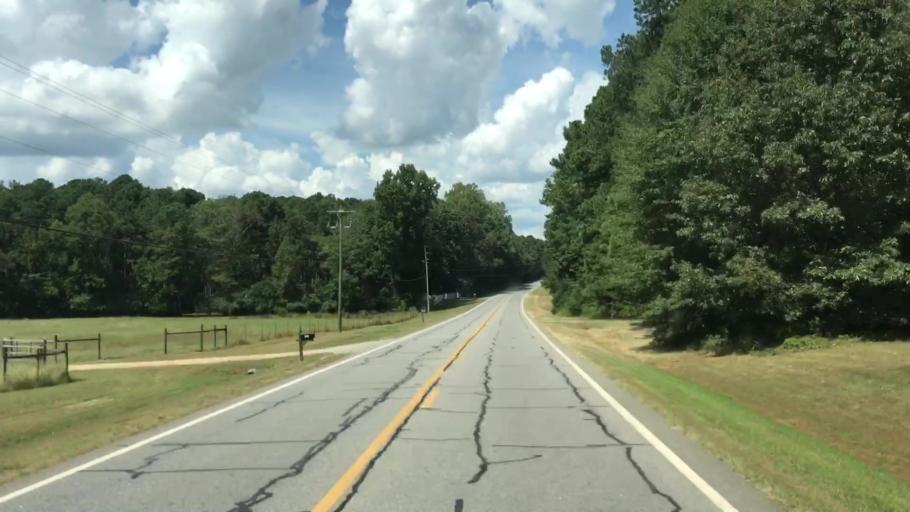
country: US
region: Georgia
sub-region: Oconee County
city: Watkinsville
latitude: 33.8095
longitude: -83.3527
